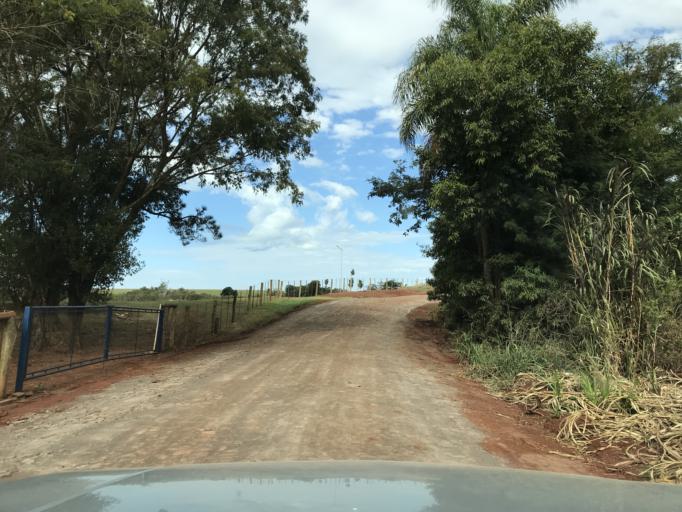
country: BR
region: Parana
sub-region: Palotina
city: Palotina
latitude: -24.3027
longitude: -53.8093
